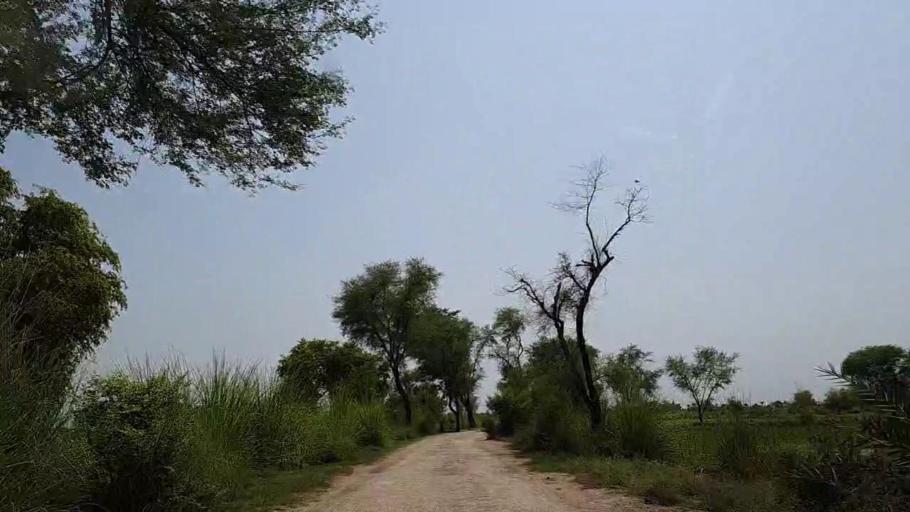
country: PK
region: Sindh
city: Adilpur
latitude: 27.9230
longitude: 69.3756
